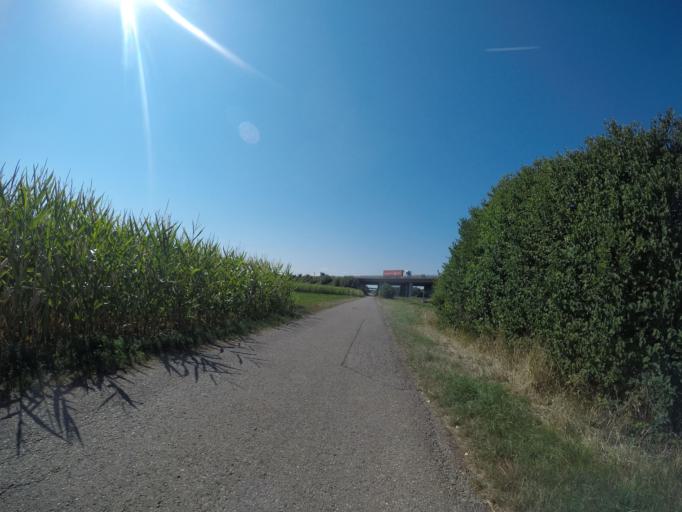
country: DE
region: Baden-Wuerttemberg
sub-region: Tuebingen Region
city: Langenau
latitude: 48.4723
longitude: 10.1131
